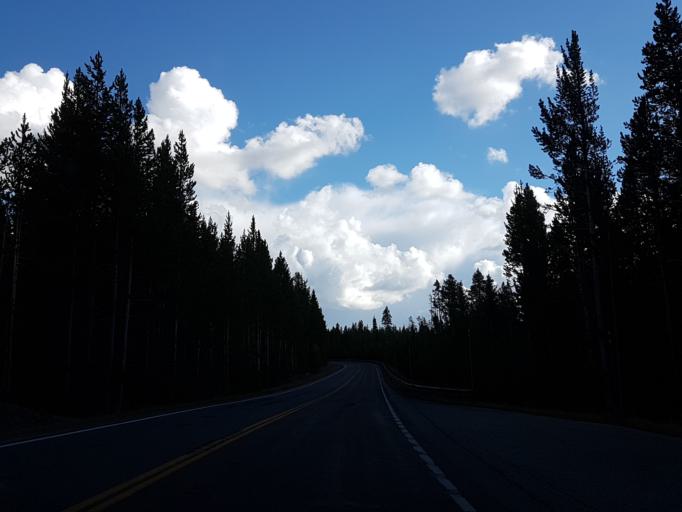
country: US
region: Montana
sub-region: Gallatin County
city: West Yellowstone
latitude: 44.4433
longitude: -110.8024
